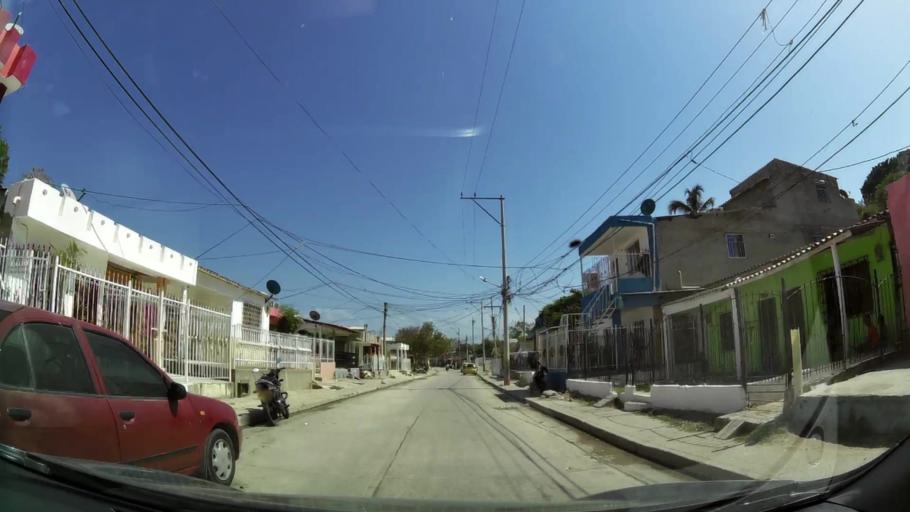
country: CO
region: Bolivar
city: Cartagena
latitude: 10.4355
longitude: -75.5198
